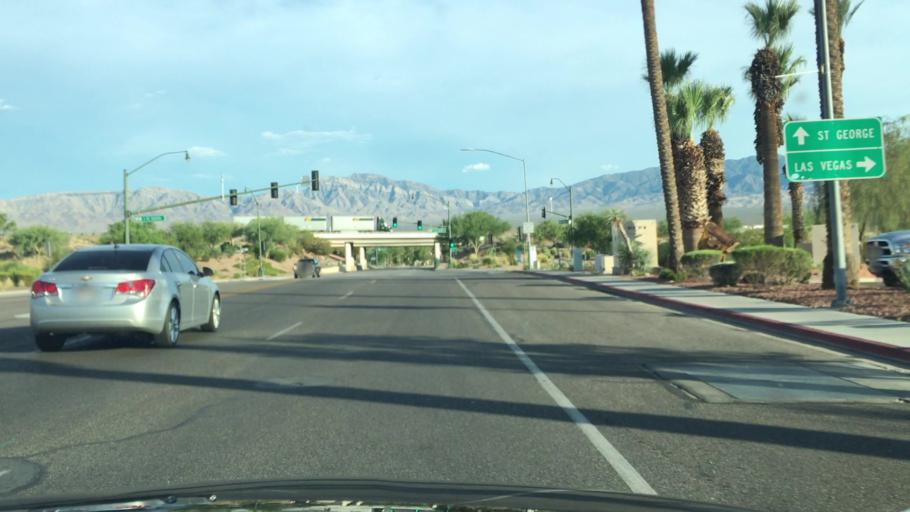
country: US
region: Nevada
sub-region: Clark County
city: Mesquite
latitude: 36.8145
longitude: -114.0651
